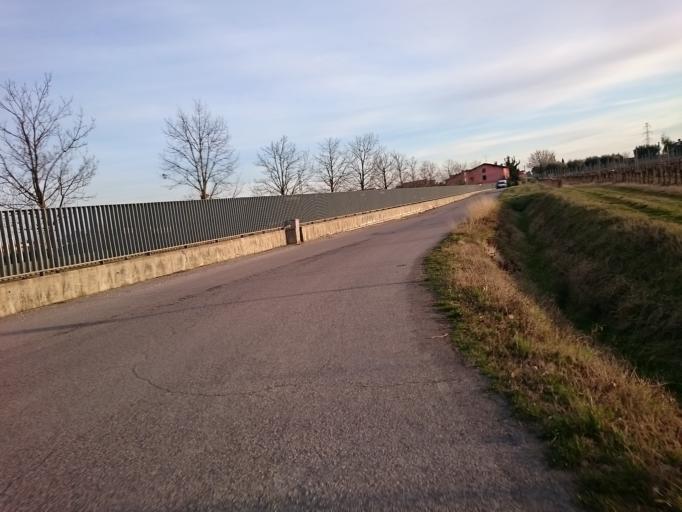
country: IT
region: Veneto
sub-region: Provincia di Verona
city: Castelnuovo del Garda
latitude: 45.4463
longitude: 10.7549
